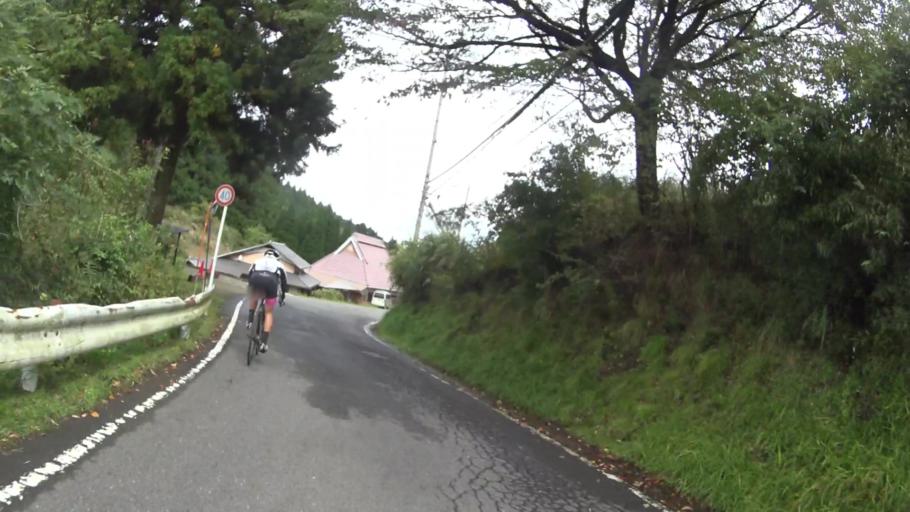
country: JP
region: Shiga Prefecture
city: Kitahama
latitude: 35.1663
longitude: 135.7811
